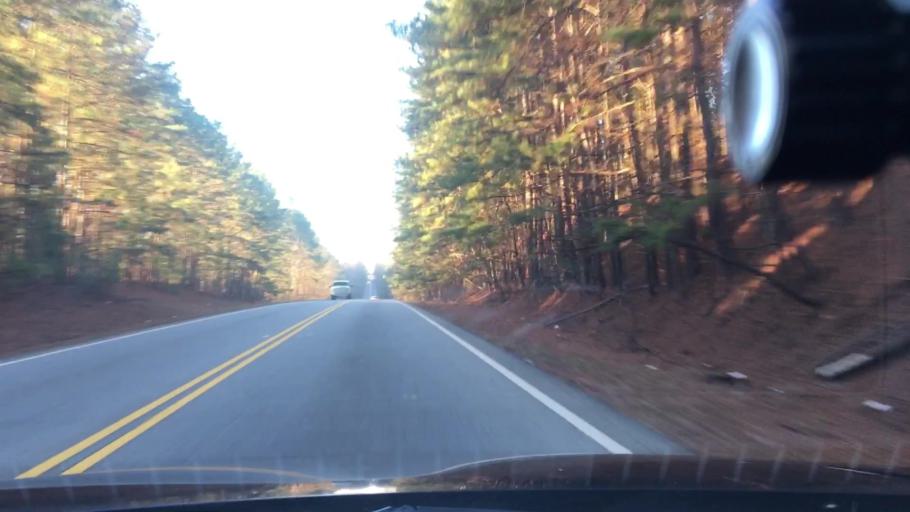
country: US
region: Georgia
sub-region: Coweta County
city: Senoia
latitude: 33.3016
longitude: -84.5374
